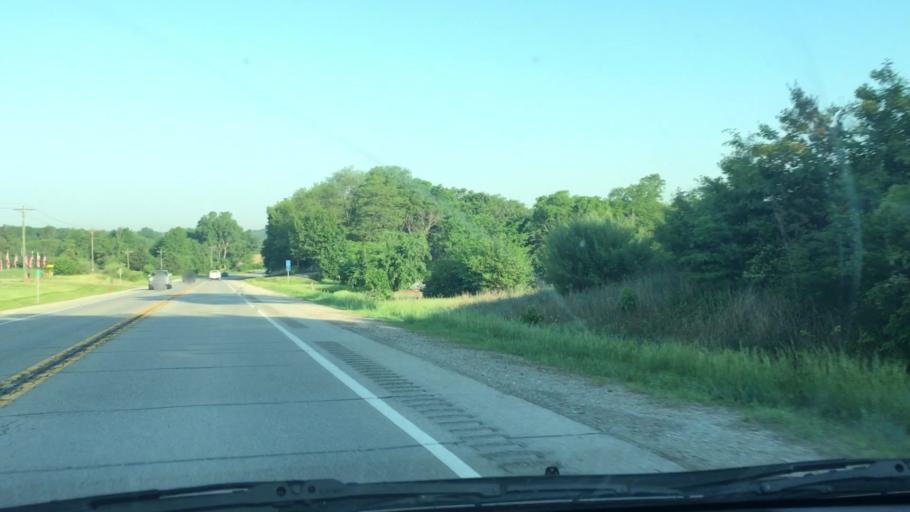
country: US
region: Iowa
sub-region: Johnson County
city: Tiffin
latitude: 41.7114
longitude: -91.6945
